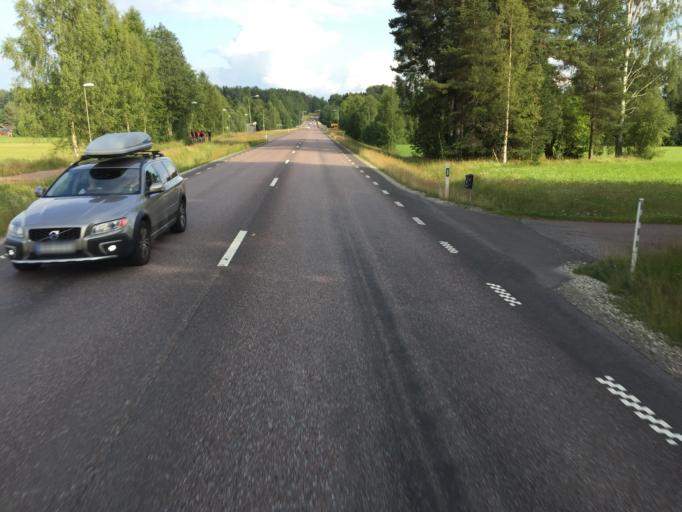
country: SE
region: Dalarna
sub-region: Borlange Kommun
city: Borlaenge
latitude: 60.5170
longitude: 15.3710
